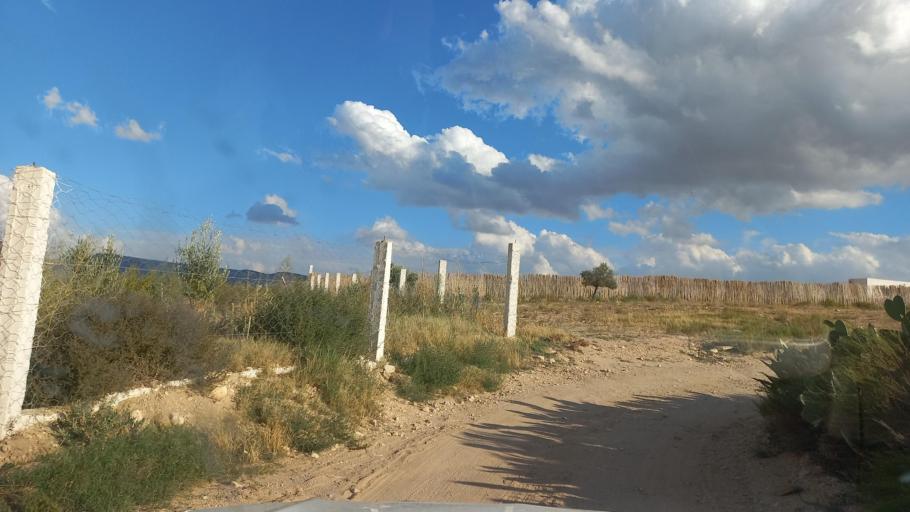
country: TN
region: Al Qasrayn
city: Sbiba
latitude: 35.3794
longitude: 9.0756
